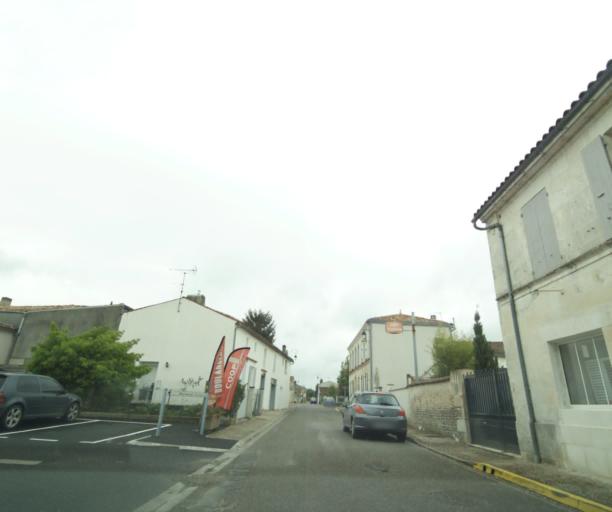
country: FR
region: Poitou-Charentes
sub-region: Departement de la Charente-Maritime
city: Perignac
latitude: 45.6484
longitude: -0.5033
